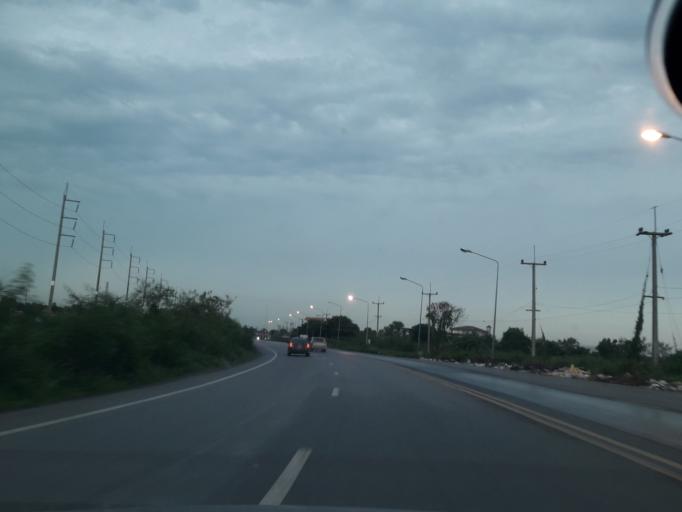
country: TH
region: Pathum Thani
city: Ban Rangsit
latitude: 14.0172
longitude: 100.7493
